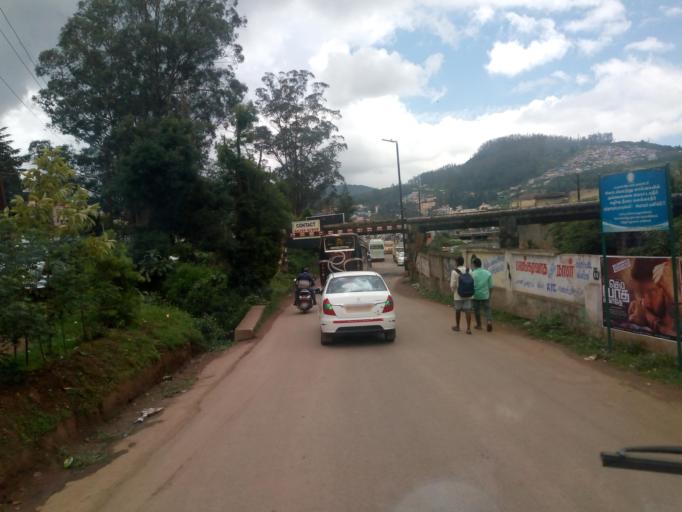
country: IN
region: Tamil Nadu
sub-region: Nilgiri
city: Ooty
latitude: 11.4045
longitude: 76.6952
